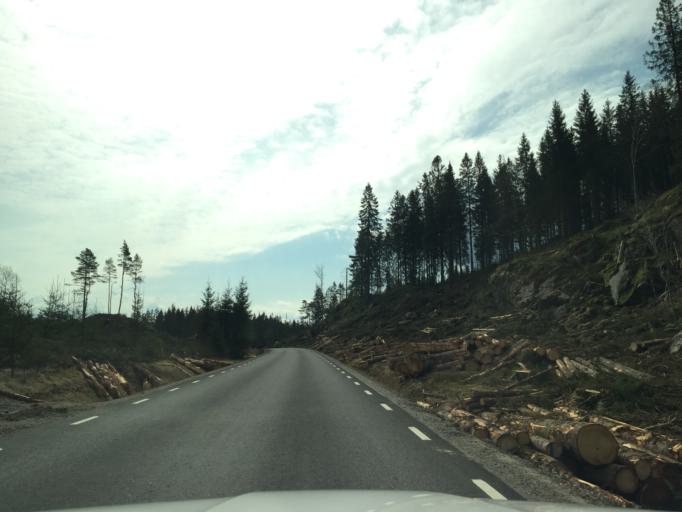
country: SE
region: Vaestra Goetaland
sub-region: Lilla Edets Kommun
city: Lodose
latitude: 58.0731
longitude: 11.9997
